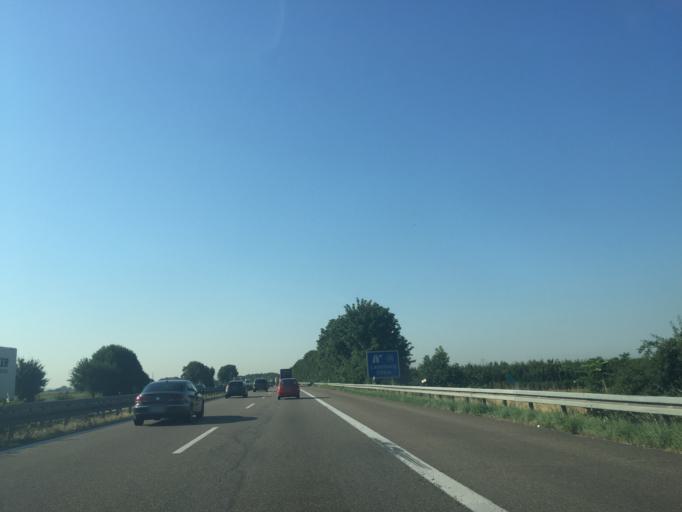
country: DE
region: Baden-Wuerttemberg
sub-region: Karlsruhe Region
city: Schriesheim
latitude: 49.4896
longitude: 8.6386
